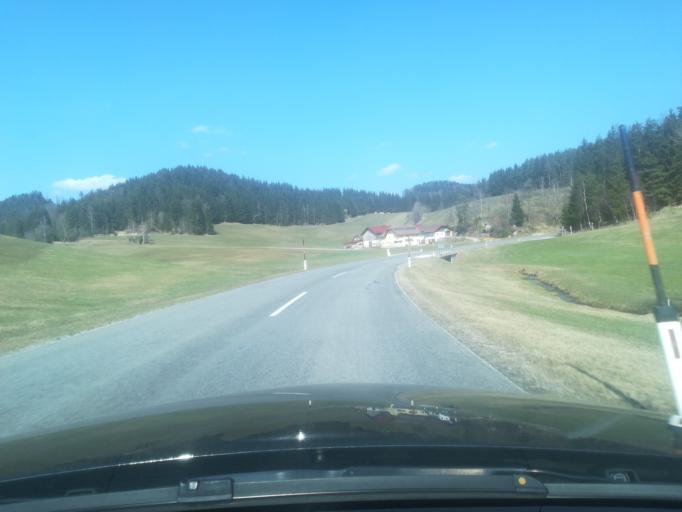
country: AT
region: Lower Austria
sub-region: Politischer Bezirk Zwettl
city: Langschlag
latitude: 48.4926
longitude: 14.8121
